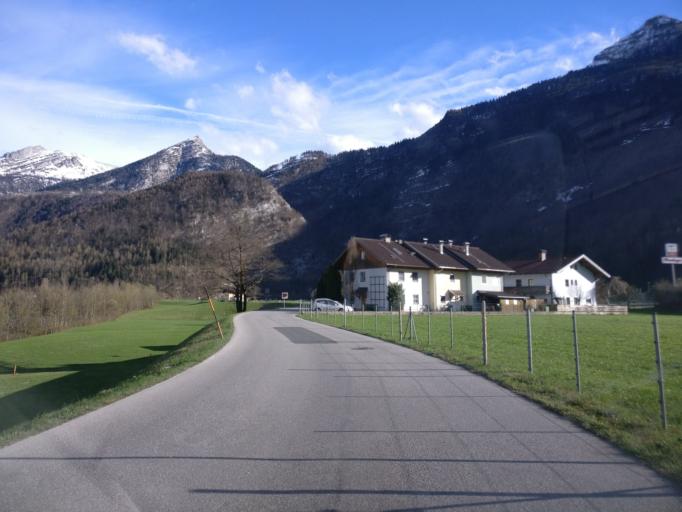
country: AT
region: Salzburg
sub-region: Politischer Bezirk Hallein
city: Golling an der Salzach
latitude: 47.5863
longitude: 13.1586
